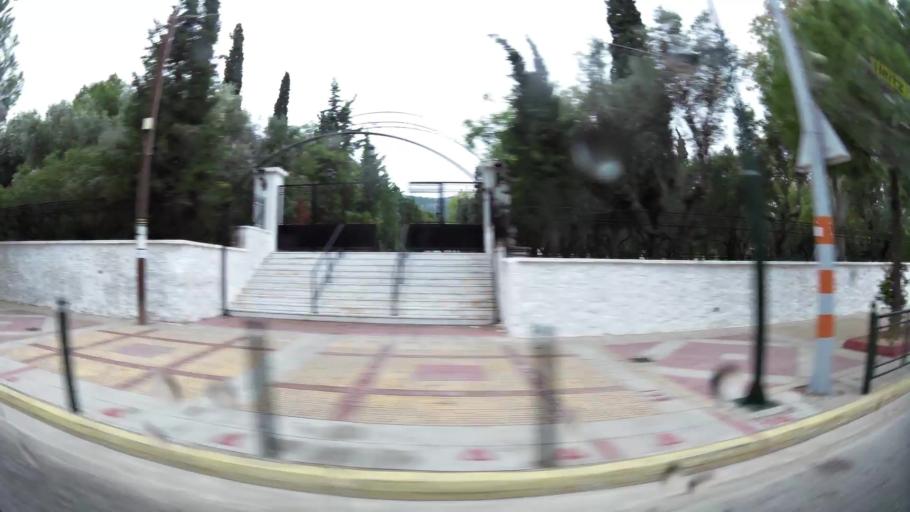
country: GR
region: Attica
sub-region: Nomarchia Athinas
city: Agia Varvara
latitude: 37.9947
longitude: 23.6613
